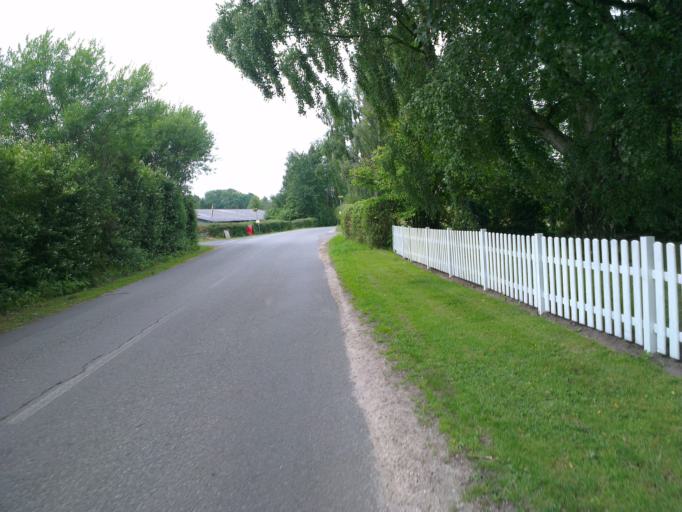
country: DK
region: Capital Region
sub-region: Frederikssund Kommune
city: Jaegerspris
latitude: 55.8126
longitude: 11.9413
